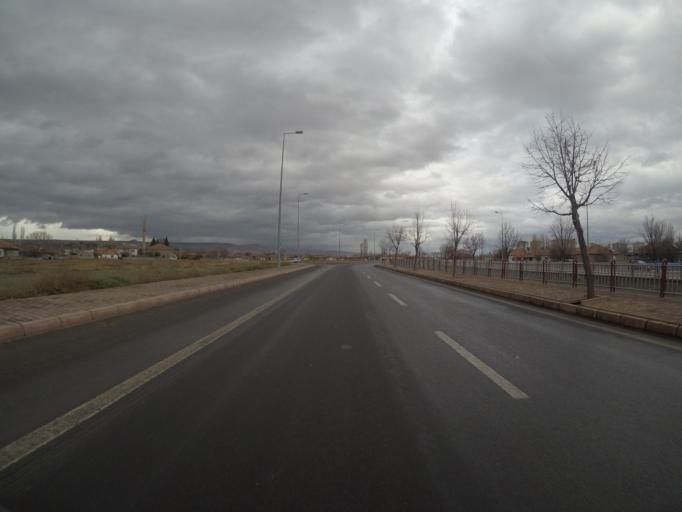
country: TR
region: Kayseri
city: Kayseri
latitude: 38.7539
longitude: 35.4769
